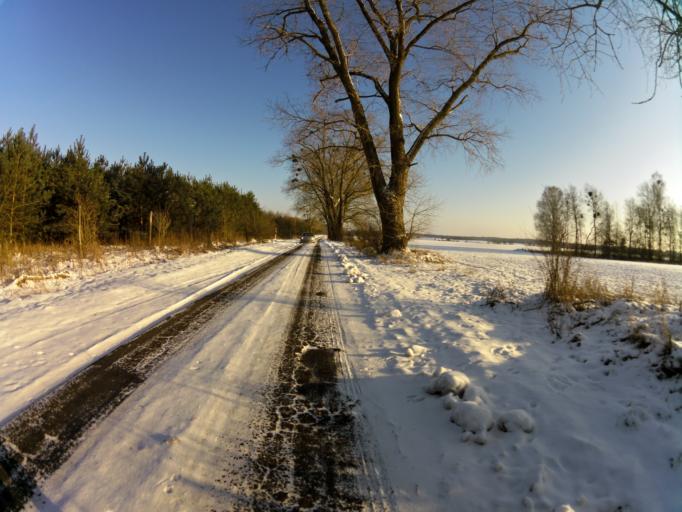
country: PL
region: West Pomeranian Voivodeship
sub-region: Powiat stargardzki
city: Dobrzany
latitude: 53.3294
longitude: 15.4196
